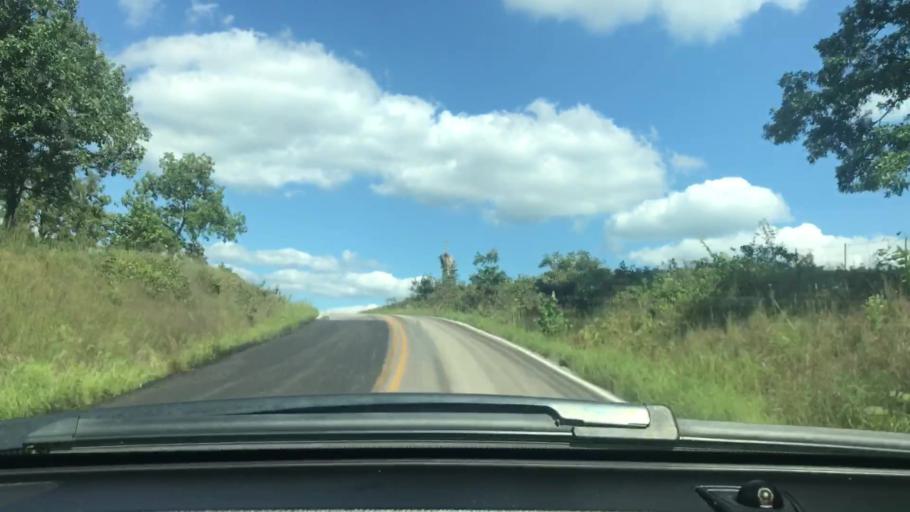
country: US
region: Missouri
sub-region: Wright County
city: Hartville
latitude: 37.3716
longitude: -92.3892
